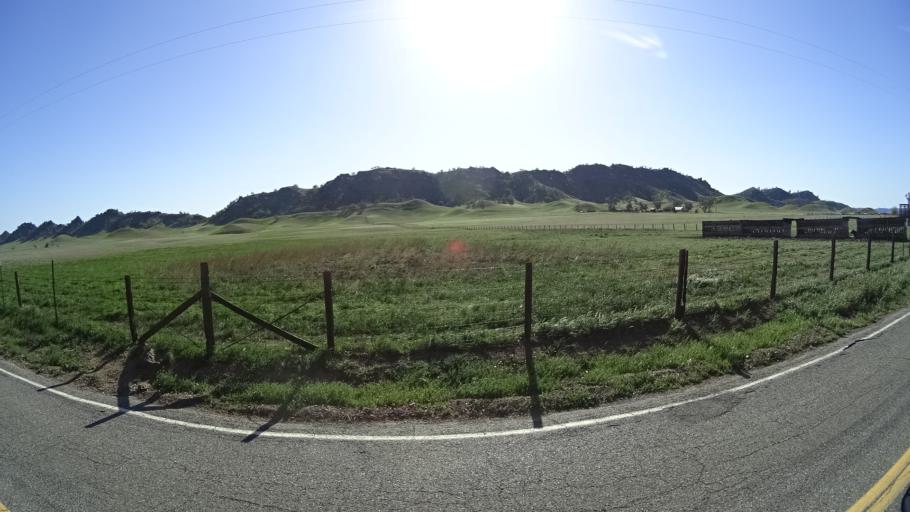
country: US
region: California
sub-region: Tehama County
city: Rancho Tehama Reserve
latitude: 39.7322
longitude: -122.5506
